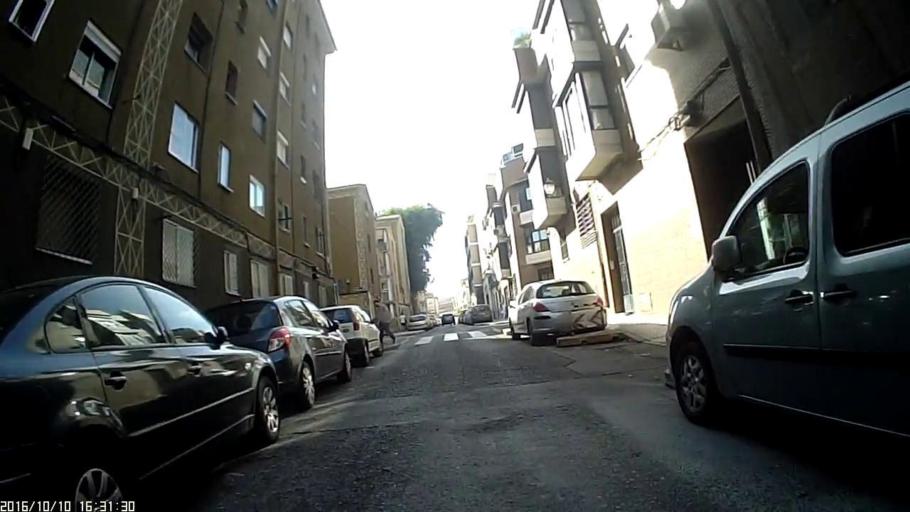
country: ES
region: Madrid
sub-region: Provincia de Madrid
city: Carabanchel
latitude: 40.4119
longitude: -3.7256
